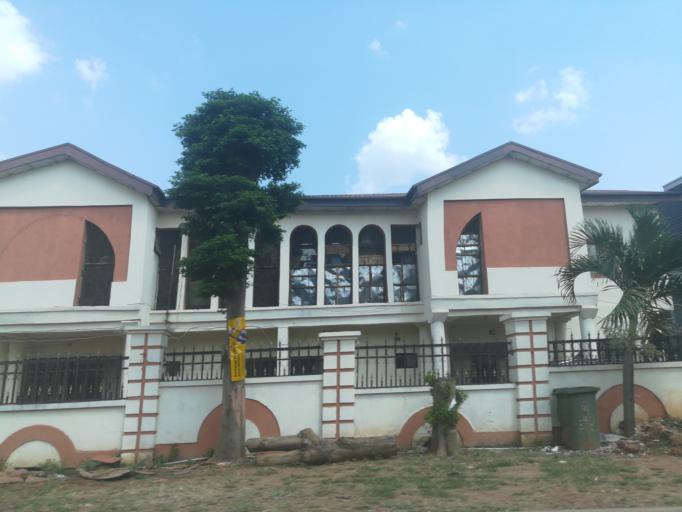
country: NG
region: Abuja Federal Capital Territory
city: Abuja
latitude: 9.0473
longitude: 7.4454
